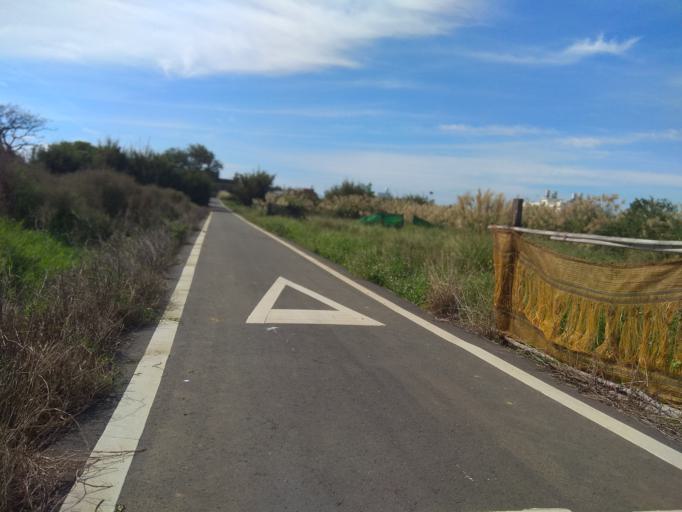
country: TW
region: Taiwan
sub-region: Hsinchu
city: Zhubei
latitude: 25.0146
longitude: 121.0763
